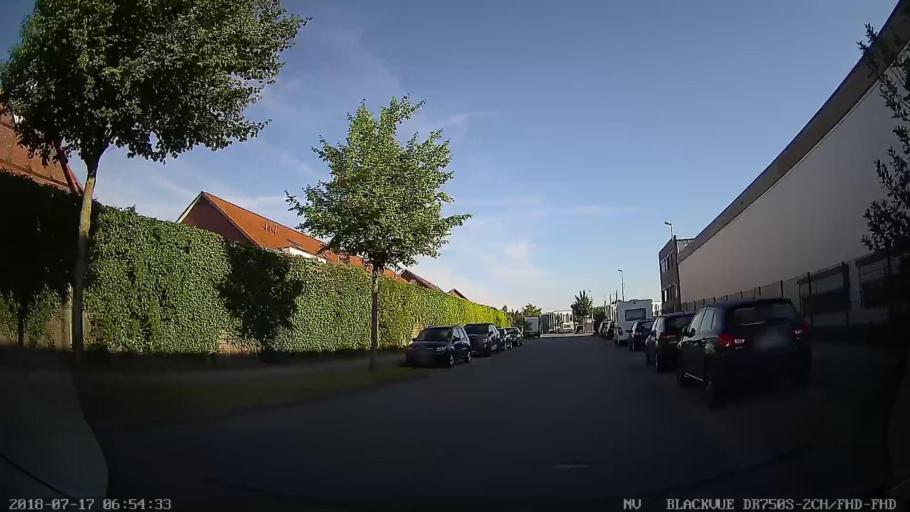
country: DE
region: Schleswig-Holstein
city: Rellingen
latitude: 53.6451
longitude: 9.8241
